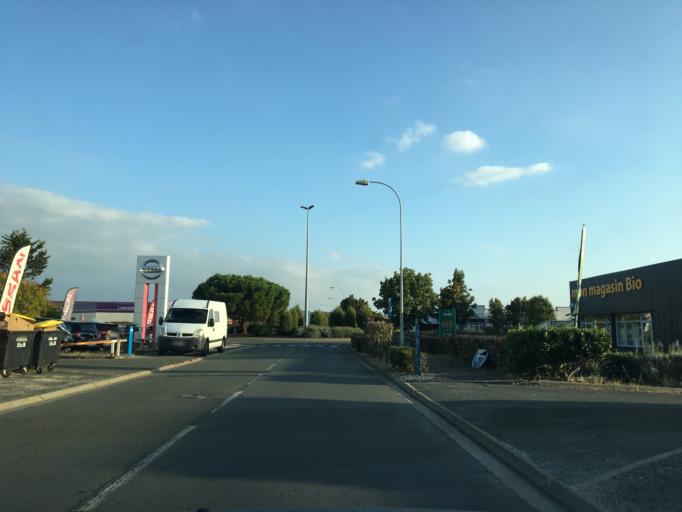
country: FR
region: Poitou-Charentes
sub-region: Departement de la Charente-Maritime
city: Angoulins
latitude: 46.1067
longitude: -1.1007
